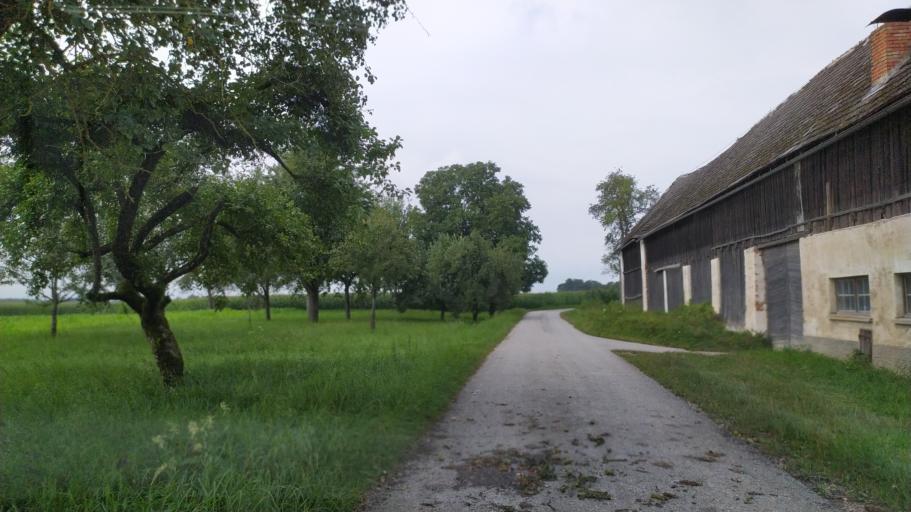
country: AT
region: Upper Austria
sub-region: Politischer Bezirk Perg
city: Bad Kreuzen
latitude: 48.1980
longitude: 14.7858
